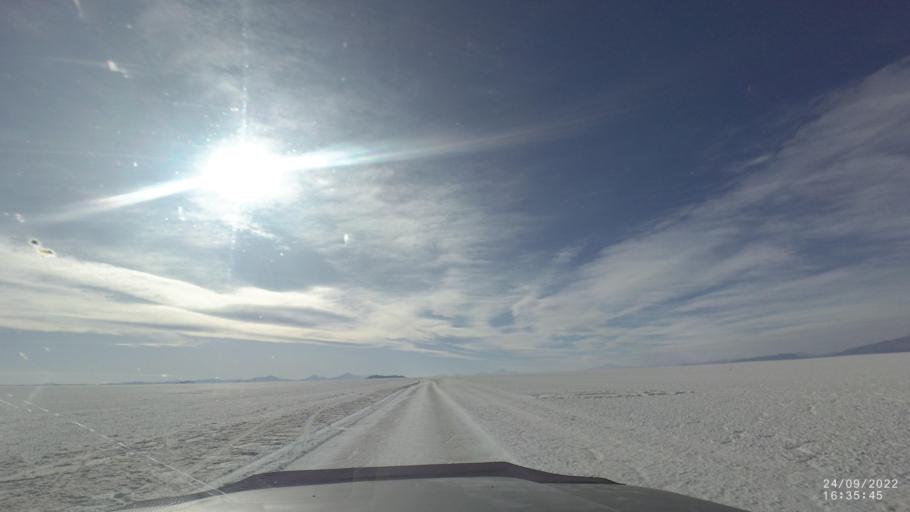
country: BO
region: Potosi
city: Colchani
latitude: -20.2377
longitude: -67.6323
